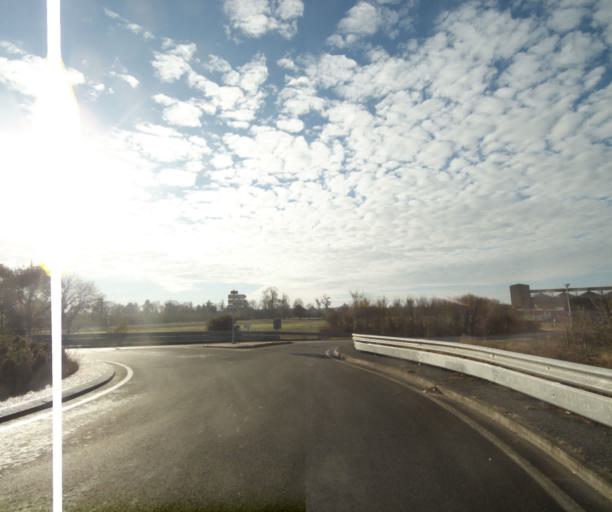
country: FR
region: Poitou-Charentes
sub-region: Departement de la Charente-Maritime
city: Corme-Royal
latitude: 45.7030
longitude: -0.7750
